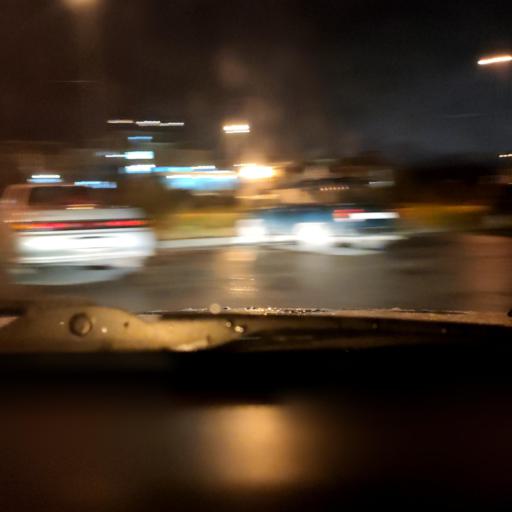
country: RU
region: Perm
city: Perm
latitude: 58.0347
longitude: 56.1769
